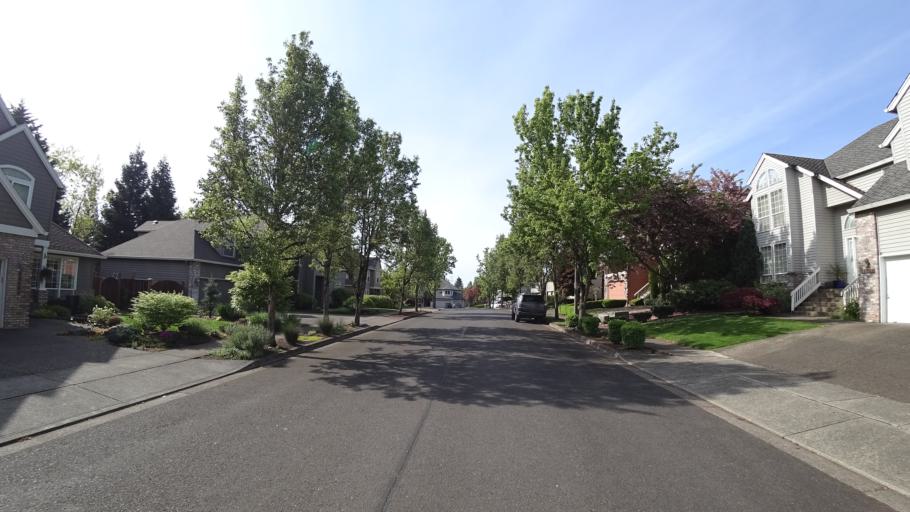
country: US
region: Oregon
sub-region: Washington County
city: Aloha
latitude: 45.4509
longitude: -122.8403
